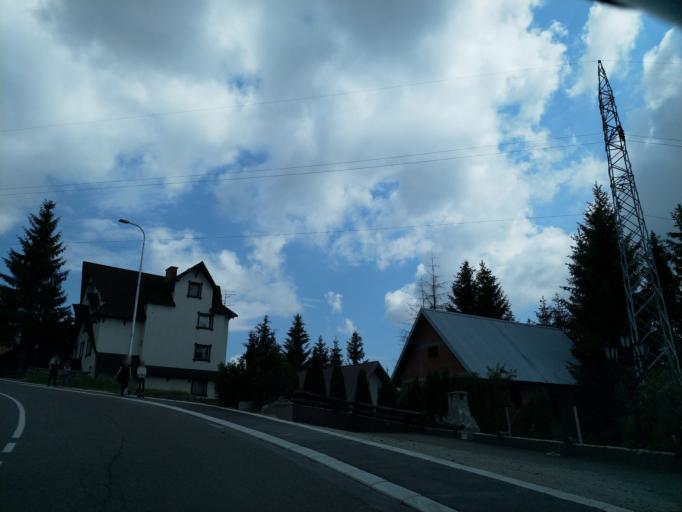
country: RS
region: Central Serbia
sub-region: Raski Okrug
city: Raska
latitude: 43.2739
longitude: 20.7813
